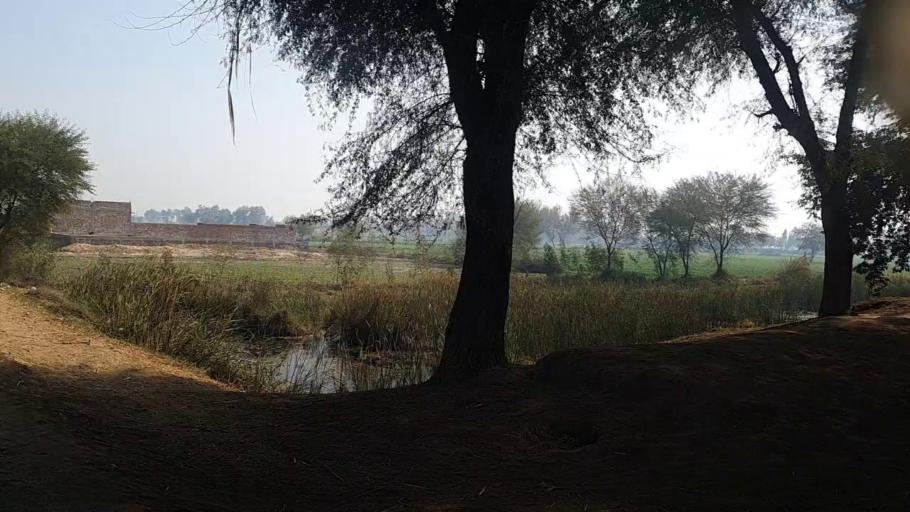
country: PK
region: Sindh
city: Khairpur
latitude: 27.9434
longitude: 69.6533
